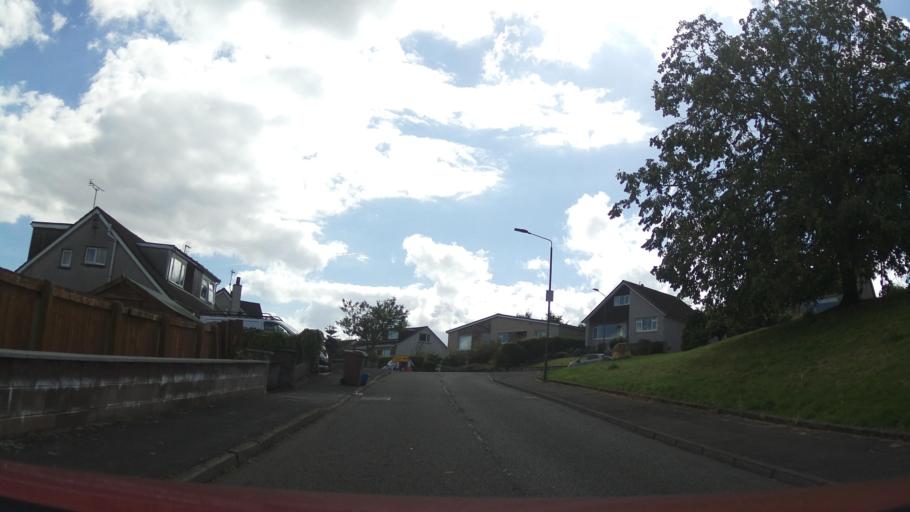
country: GB
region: Scotland
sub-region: Stirling
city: Dunblane
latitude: 56.1841
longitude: -3.9714
